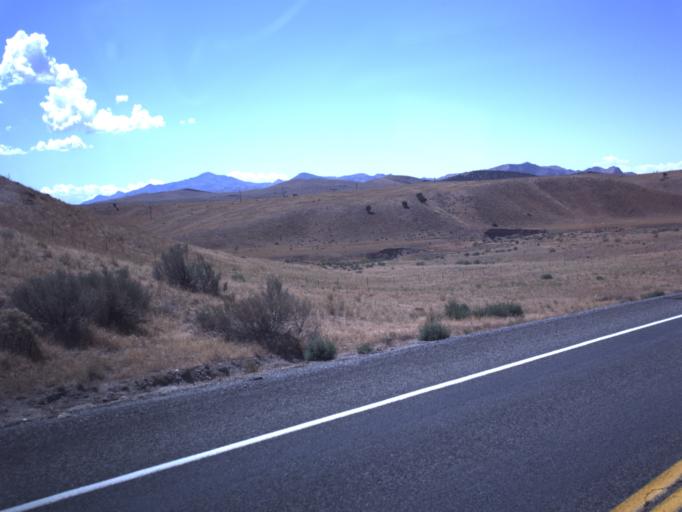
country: US
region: Utah
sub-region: Juab County
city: Nephi
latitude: 39.6406
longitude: -112.0882
